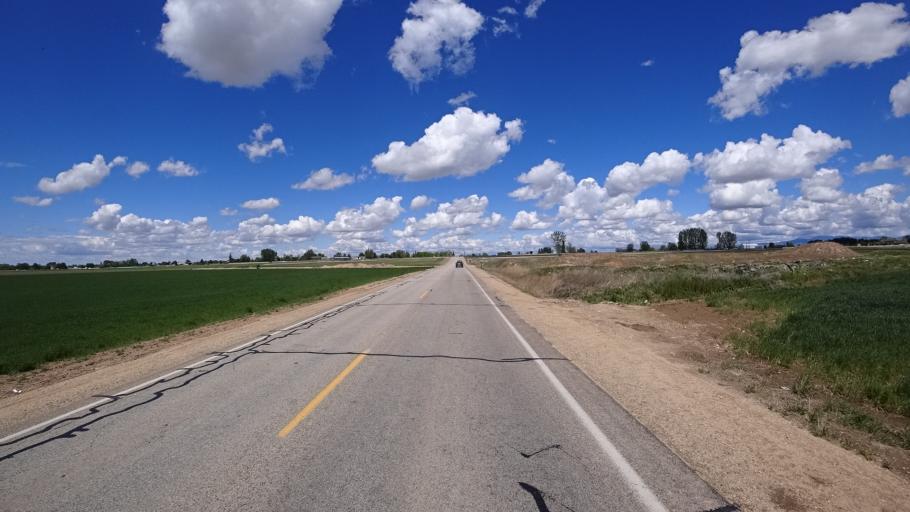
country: US
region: Idaho
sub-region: Ada County
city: Meridian
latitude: 43.5705
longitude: -116.4338
